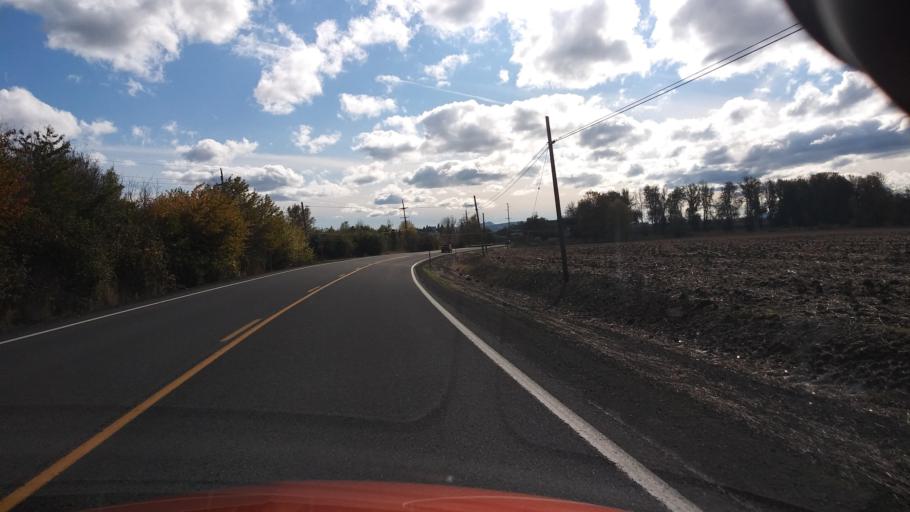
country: US
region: Oregon
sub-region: Washington County
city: Banks
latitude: 45.5761
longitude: -123.1100
